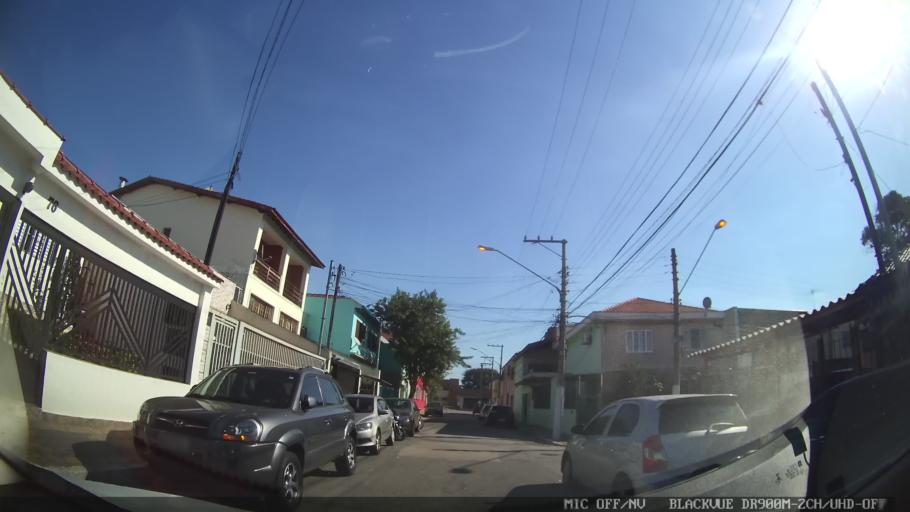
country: BR
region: Sao Paulo
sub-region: Sao Paulo
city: Sao Paulo
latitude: -23.4913
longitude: -46.6490
